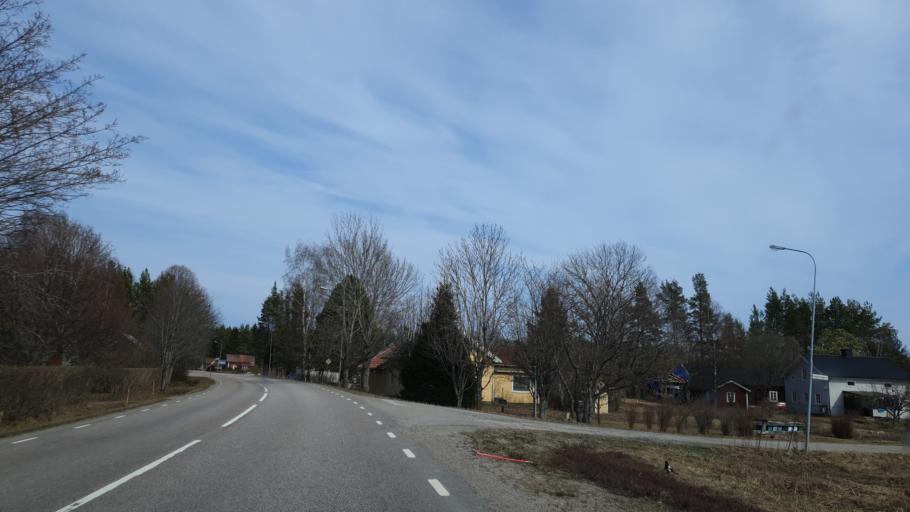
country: SE
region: Gaevleborg
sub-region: Gavle Kommun
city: Norrsundet
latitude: 61.0029
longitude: 17.1244
